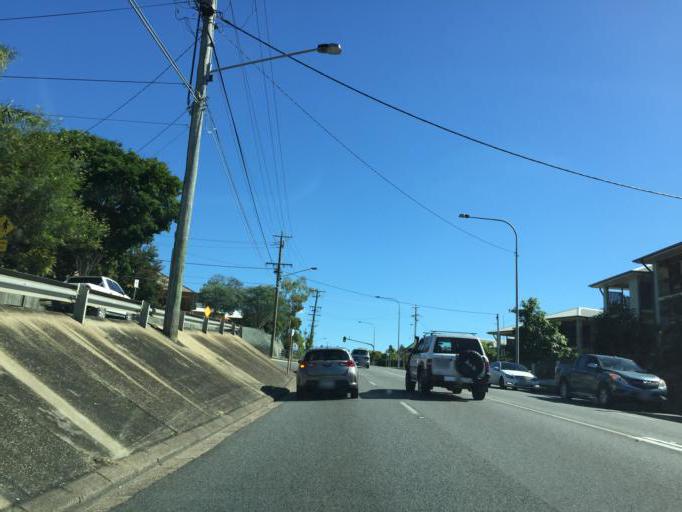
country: AU
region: Queensland
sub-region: Brisbane
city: Everton Park
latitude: -27.4146
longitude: 152.9764
